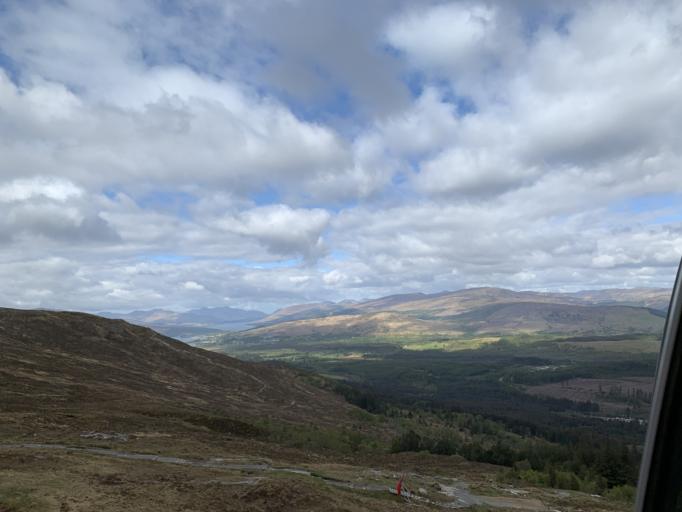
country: GB
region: Scotland
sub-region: Highland
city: Spean Bridge
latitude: 56.8423
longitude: -4.9822
